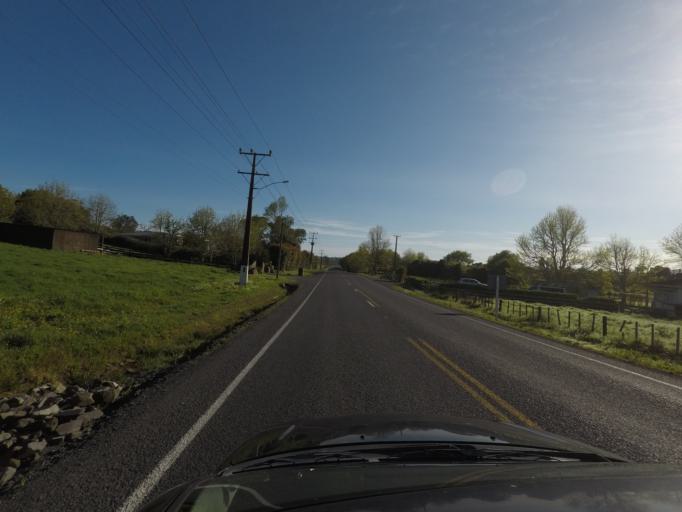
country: NZ
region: Auckland
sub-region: Auckland
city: Red Hill
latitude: -37.0120
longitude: 174.9508
